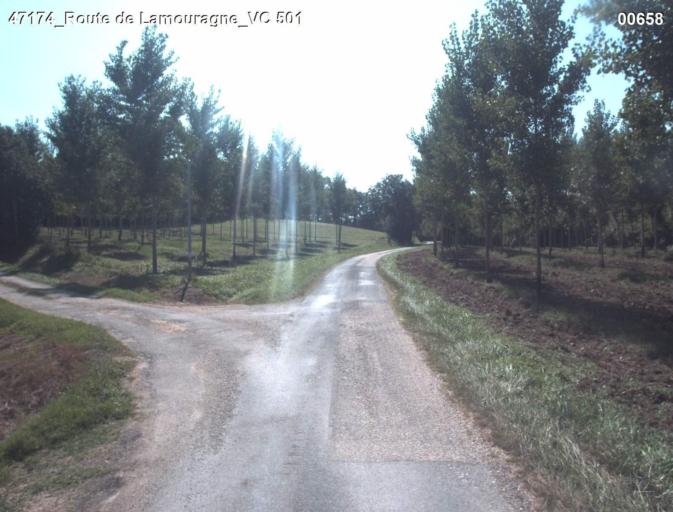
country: FR
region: Midi-Pyrenees
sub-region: Departement du Gers
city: Condom
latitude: 44.0418
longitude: 0.3864
